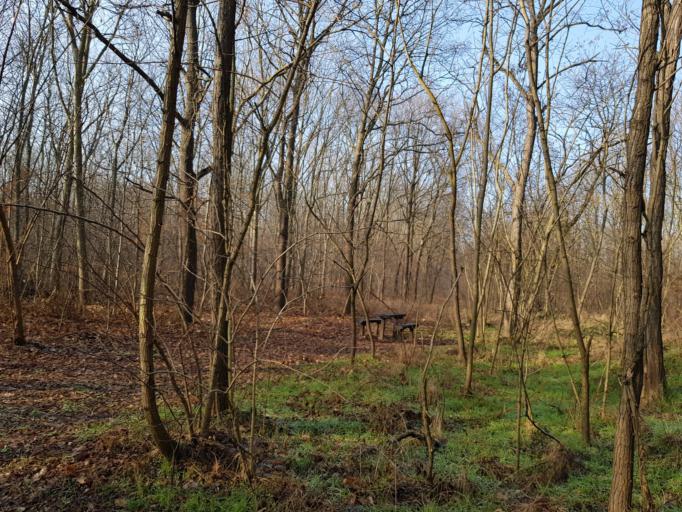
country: HU
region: Budapest
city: Budapest XVIII. keruelet
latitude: 47.4697
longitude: 19.2103
